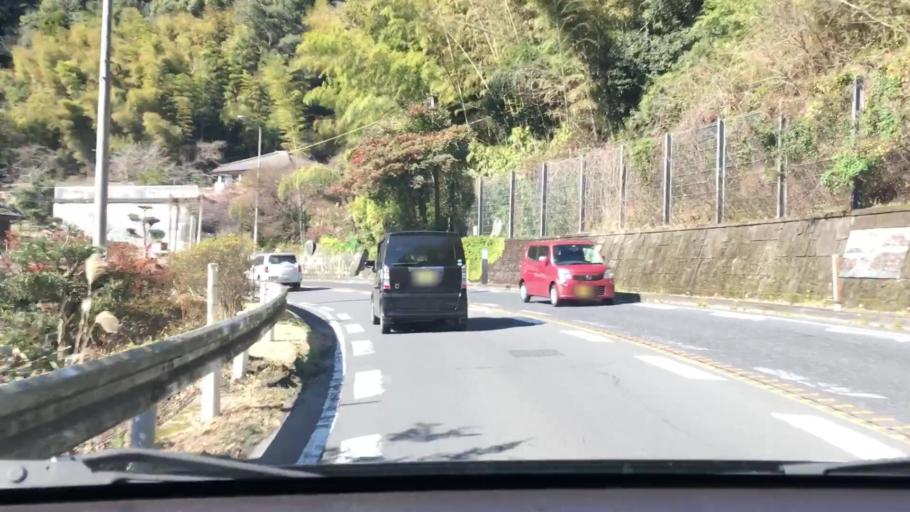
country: JP
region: Kagoshima
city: Kagoshima-shi
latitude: 31.6532
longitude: 130.5069
